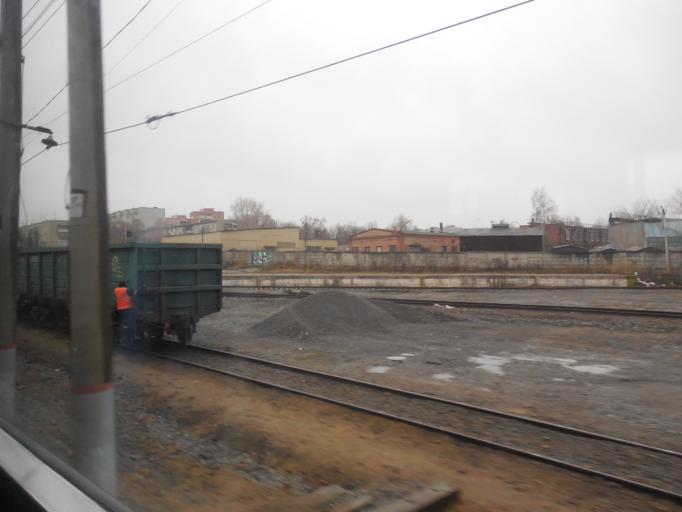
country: RU
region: Moskovskaya
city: Domodedovo
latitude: 55.4461
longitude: 37.7684
